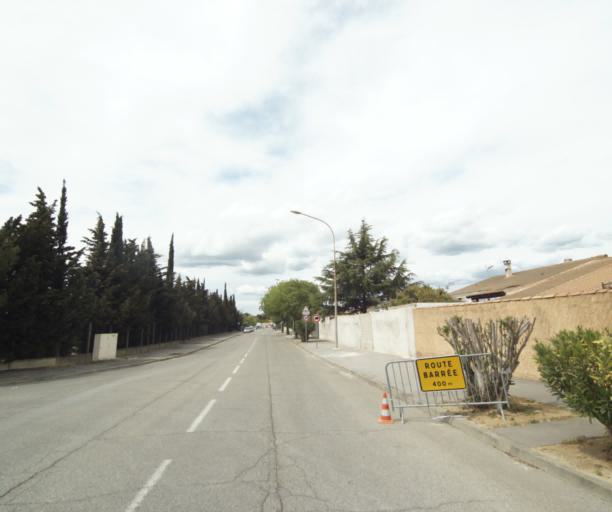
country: FR
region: Provence-Alpes-Cote d'Azur
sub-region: Departement des Bouches-du-Rhone
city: Rognac
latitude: 43.4808
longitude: 5.2354
